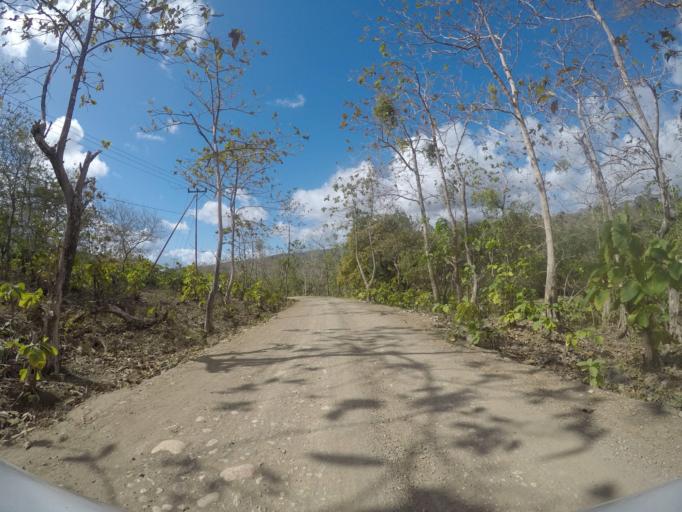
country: TL
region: Lautem
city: Lospalos
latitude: -8.5253
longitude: 126.8417
